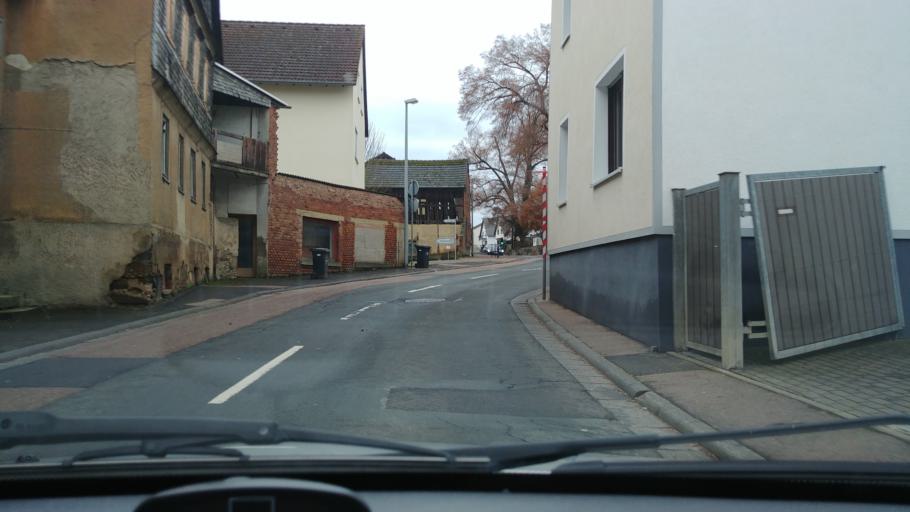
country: DE
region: Hesse
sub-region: Regierungsbezirk Giessen
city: Villmar
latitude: 50.3272
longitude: 8.1749
